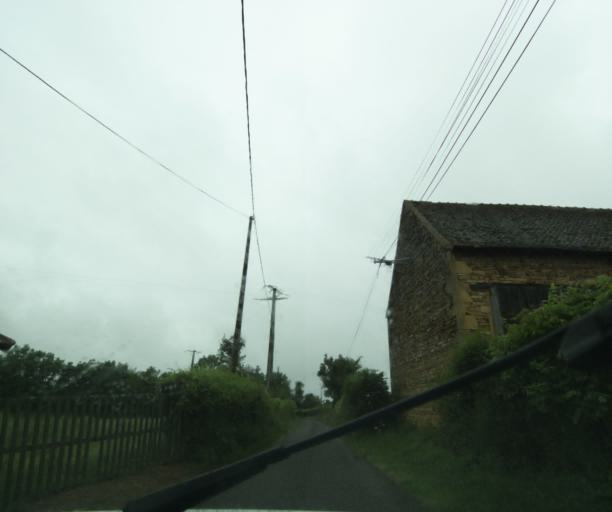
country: FR
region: Bourgogne
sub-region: Departement de Saone-et-Loire
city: Charolles
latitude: 46.3536
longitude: 4.2185
